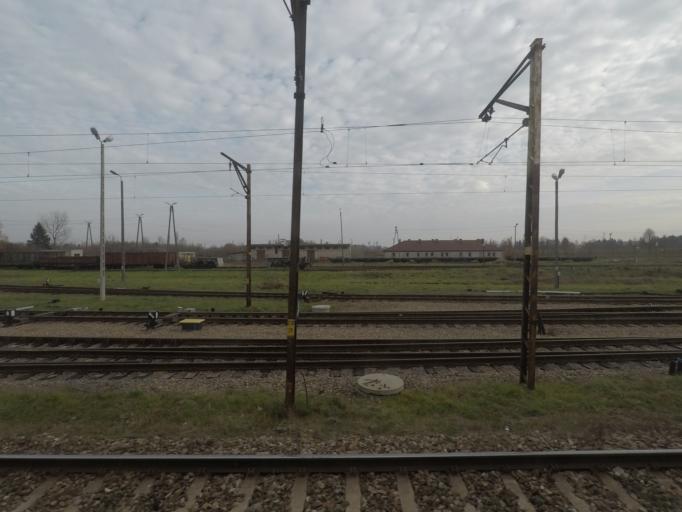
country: PL
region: Subcarpathian Voivodeship
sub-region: Powiat przemyski
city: Zurawica
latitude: 49.8265
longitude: 22.8333
